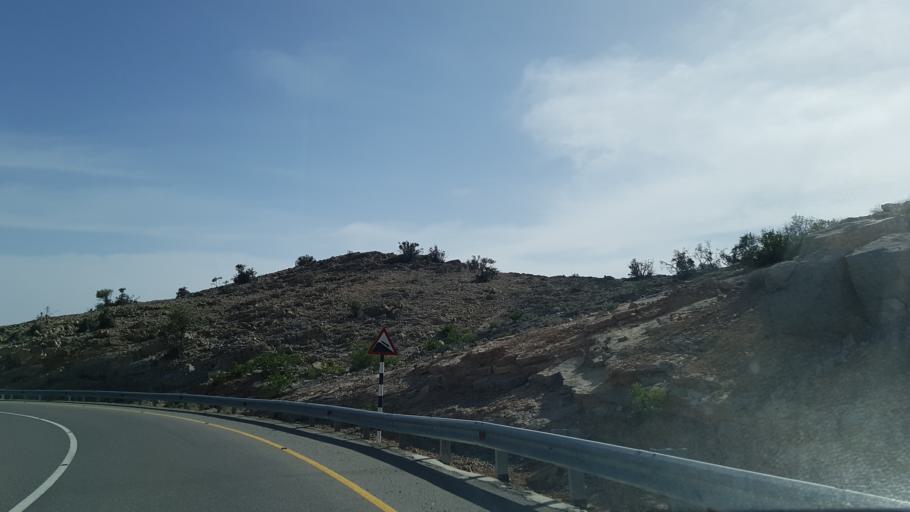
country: OM
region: Muhafazat ad Dakhiliyah
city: Izki
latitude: 23.0448
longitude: 57.7090
